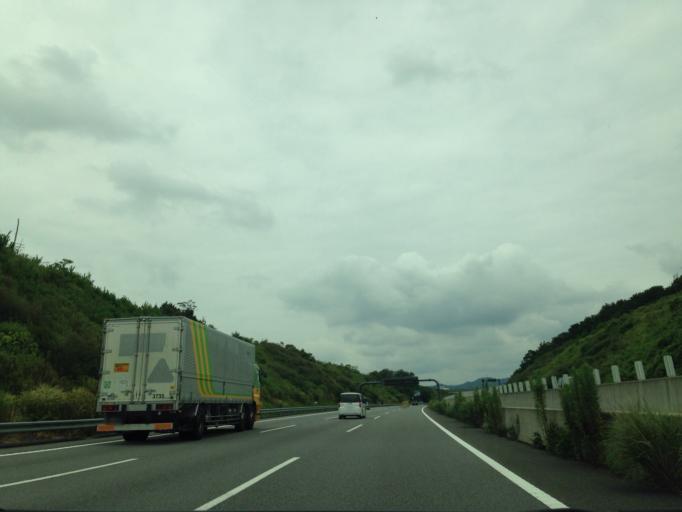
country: JP
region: Shizuoka
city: Hamakita
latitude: 34.8376
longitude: 137.7716
